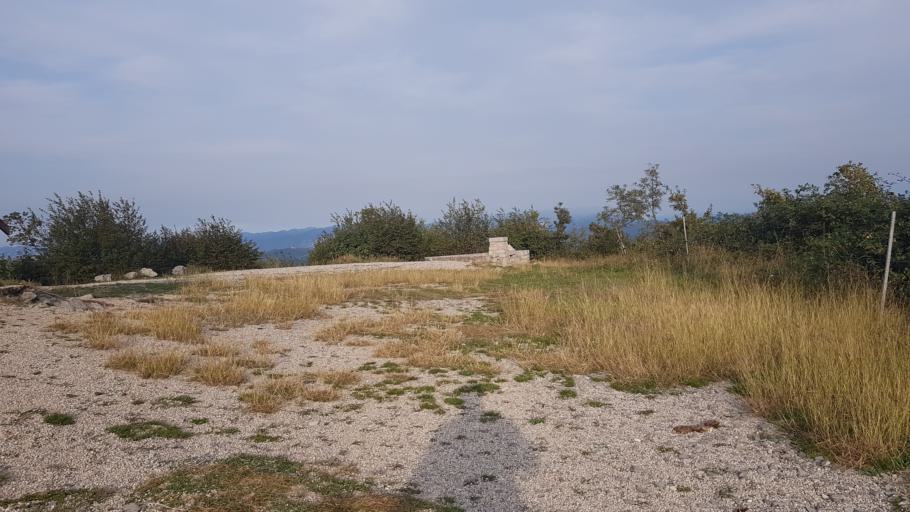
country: IT
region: Friuli Venezia Giulia
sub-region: Provincia di Trieste
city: Sgonico
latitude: 45.7470
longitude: 13.7821
